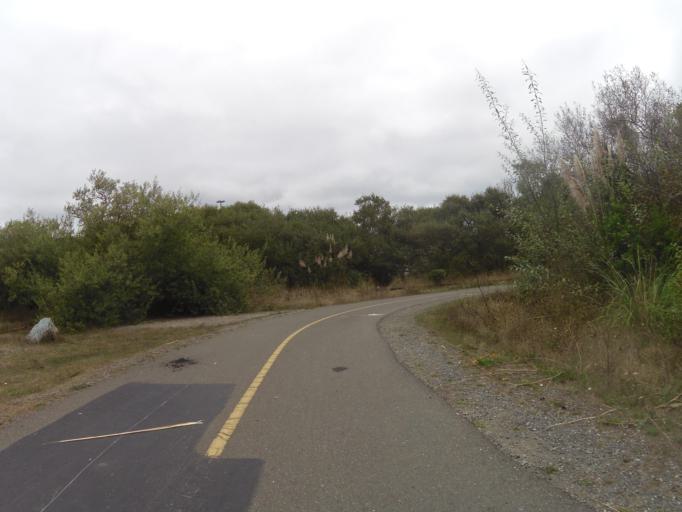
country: US
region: California
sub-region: Humboldt County
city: Bayview
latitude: 40.7787
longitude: -124.1929
